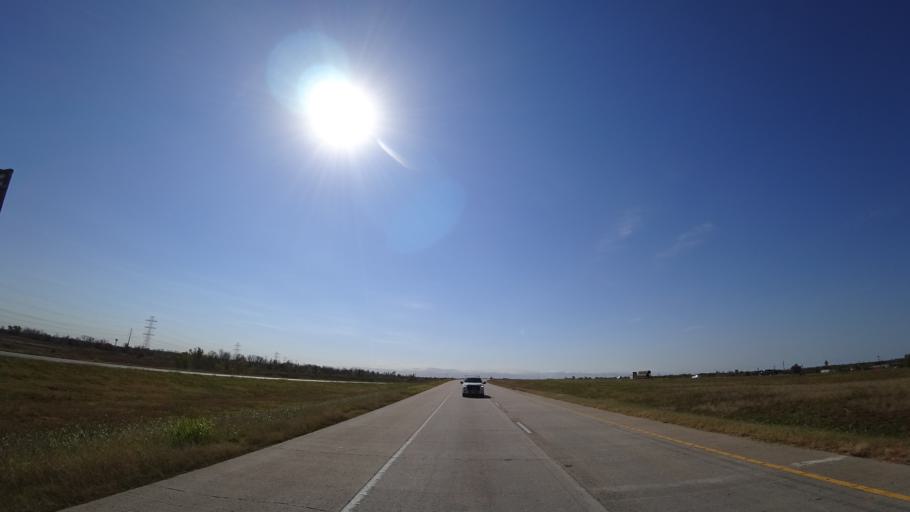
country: US
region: Texas
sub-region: Travis County
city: Hornsby Bend
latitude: 30.2320
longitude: -97.6178
